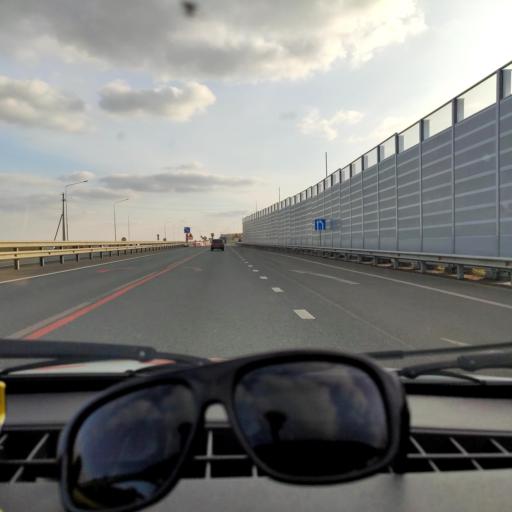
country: RU
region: Bashkortostan
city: Tolbazy
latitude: 54.1556
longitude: 55.9021
